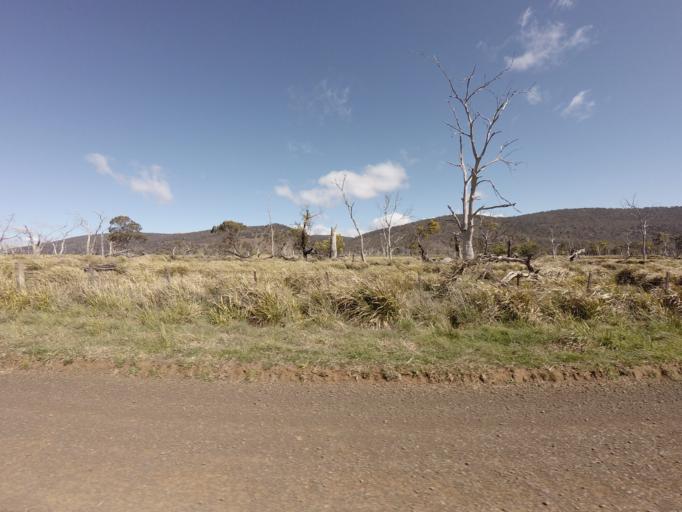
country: AU
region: Tasmania
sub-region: Northern Midlands
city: Evandale
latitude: -41.9459
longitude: 147.4309
